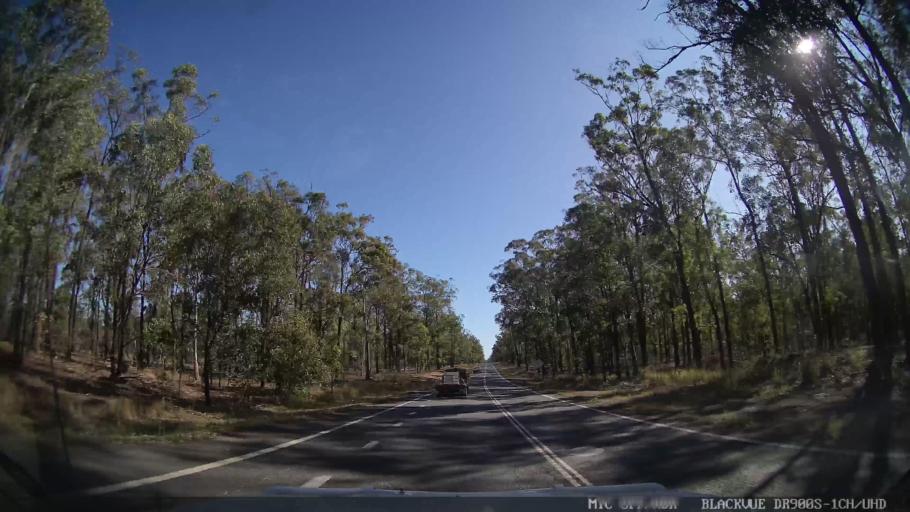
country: AU
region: Queensland
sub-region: Bundaberg
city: Childers
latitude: -25.2157
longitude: 152.0770
